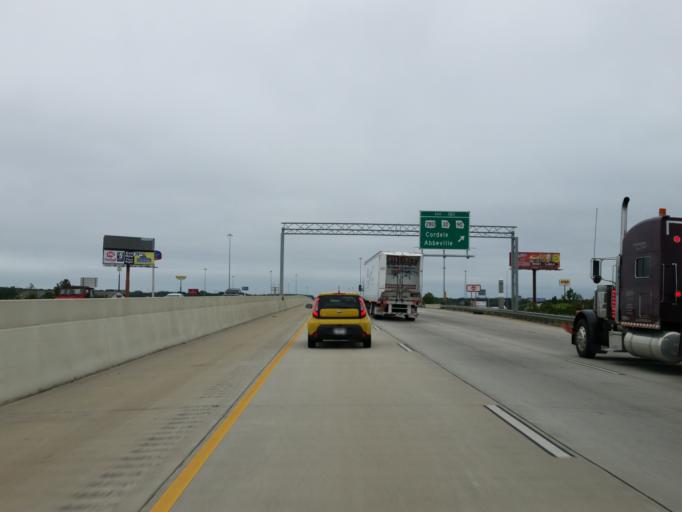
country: US
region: Georgia
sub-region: Crisp County
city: Cordele
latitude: 31.9644
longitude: -83.7523
